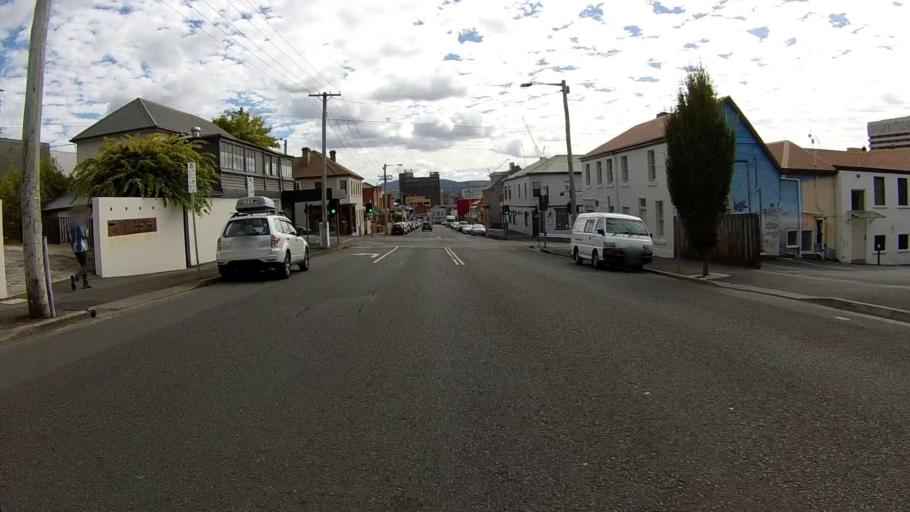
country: AU
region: Tasmania
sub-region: Hobart
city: Sandy Bay
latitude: -42.8853
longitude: 147.3212
